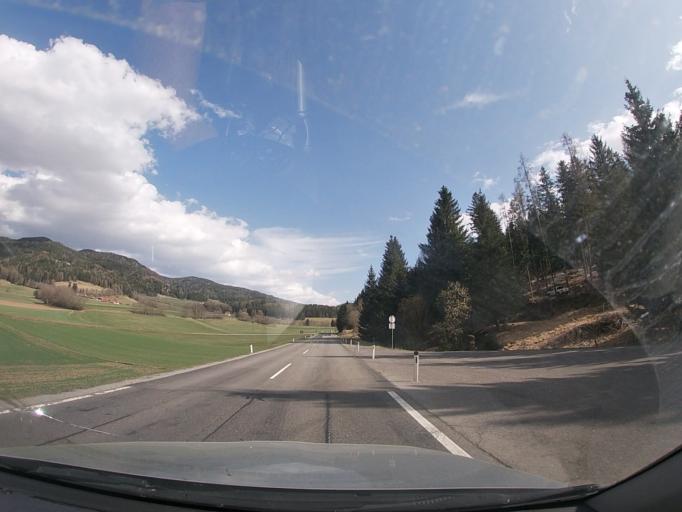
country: AT
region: Styria
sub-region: Politischer Bezirk Murau
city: Perchau am Sattel
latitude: 47.1151
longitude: 14.4547
